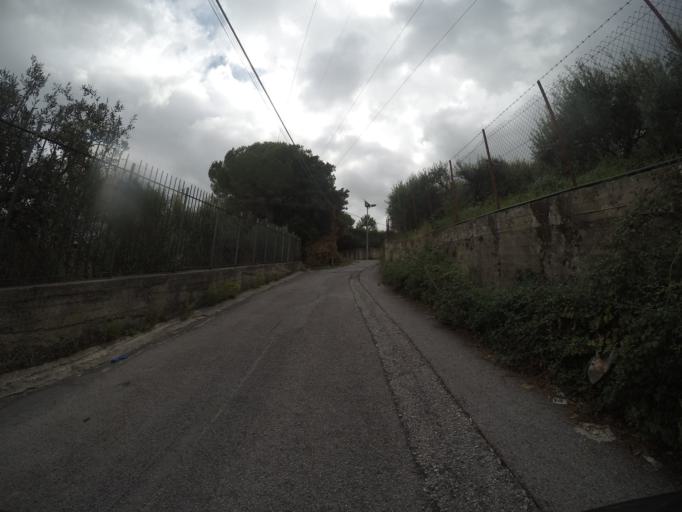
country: IT
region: Sicily
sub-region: Palermo
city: Carini
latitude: 38.1233
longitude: 13.1839
